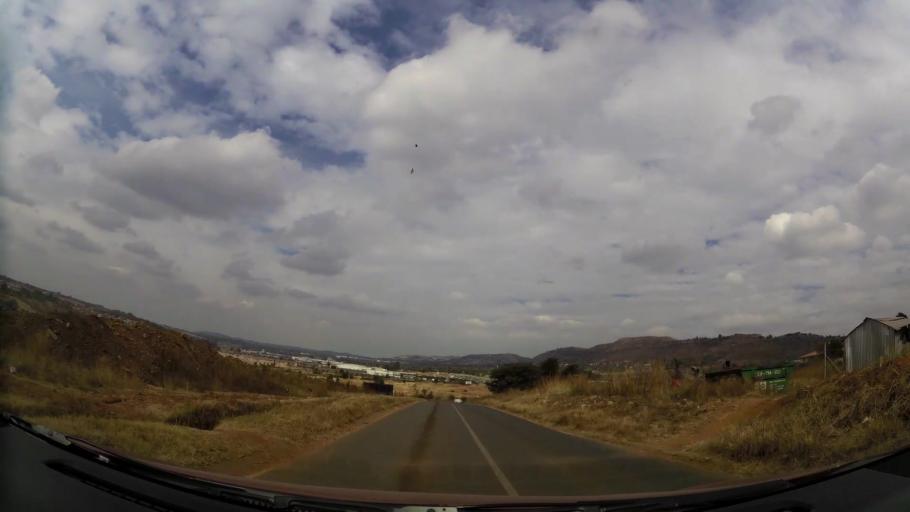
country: ZA
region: Gauteng
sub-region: City of Johannesburg Metropolitan Municipality
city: Roodepoort
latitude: -26.1039
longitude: 27.8814
